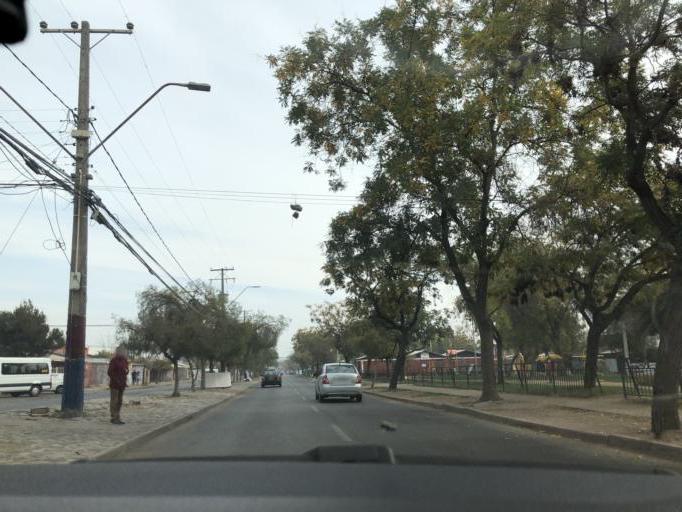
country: CL
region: Santiago Metropolitan
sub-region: Provincia de Cordillera
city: Puente Alto
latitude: -33.5939
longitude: -70.5738
